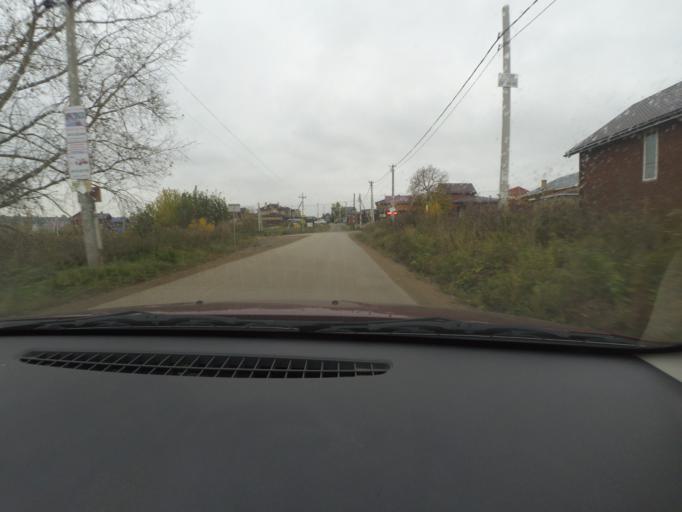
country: RU
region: Nizjnij Novgorod
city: Afonino
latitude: 56.2706
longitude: 44.0609
